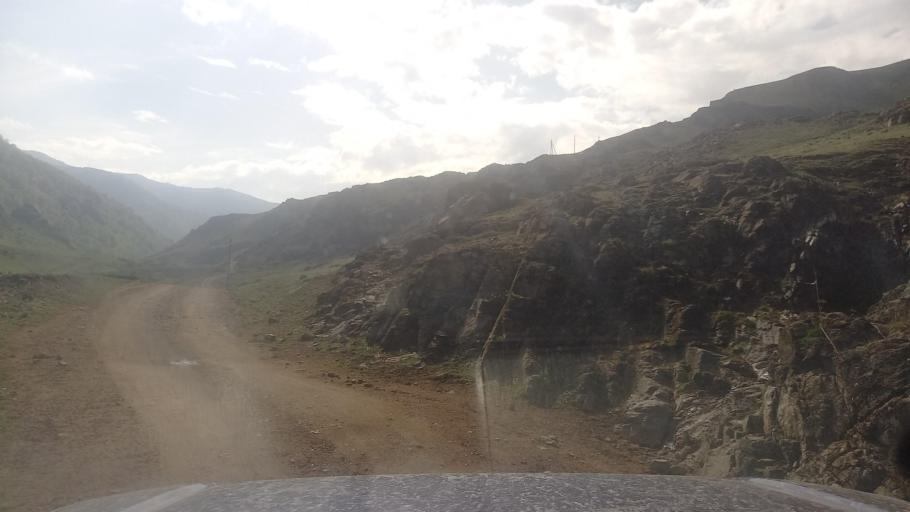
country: RU
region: Kabardino-Balkariya
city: Kamennomostskoye
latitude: 43.7249
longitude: 42.9091
